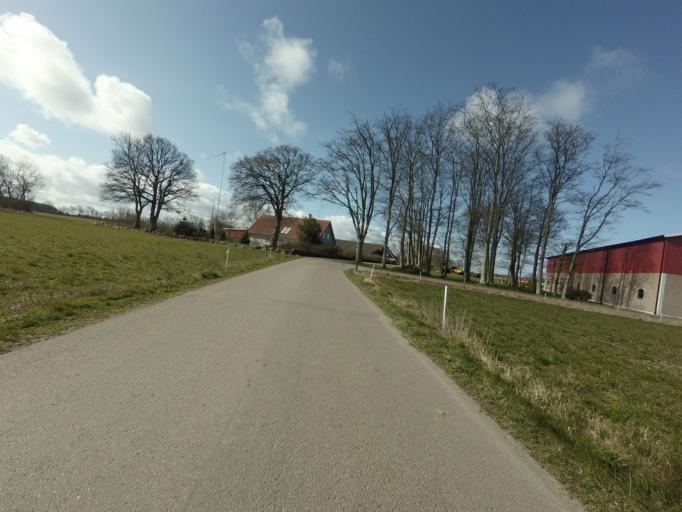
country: SE
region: Skane
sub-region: Hoganas Kommun
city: Hoganas
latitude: 56.1861
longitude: 12.6188
